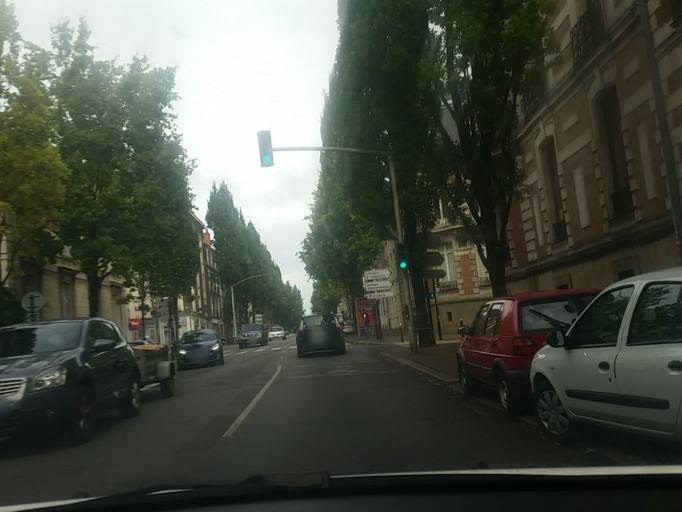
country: FR
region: Pays de la Loire
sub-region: Departement de la Loire-Atlantique
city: Nantes
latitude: 47.2246
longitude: -1.5585
